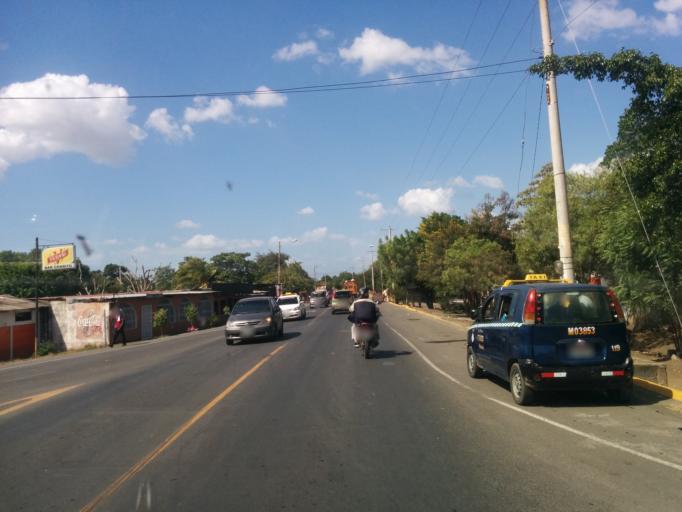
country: NI
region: Managua
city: Tipitapa
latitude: 12.1912
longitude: -86.0971
